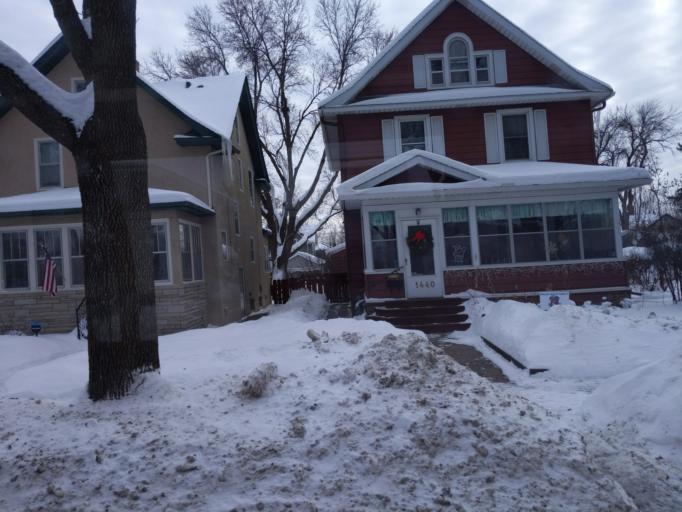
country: US
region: Minnesota
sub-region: Ramsey County
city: Falcon Heights
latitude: 44.9629
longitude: -93.1612
